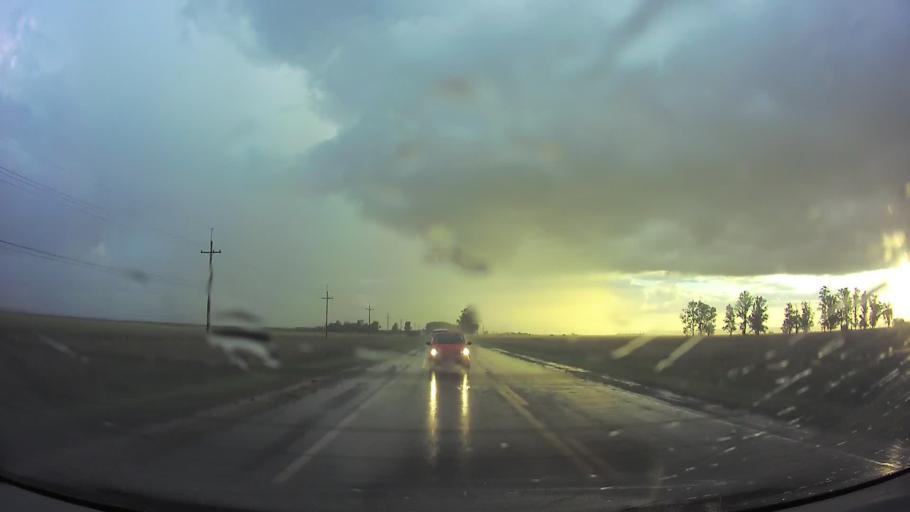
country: PY
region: Paraguari
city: Paraguari
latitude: -25.6546
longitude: -57.1603
